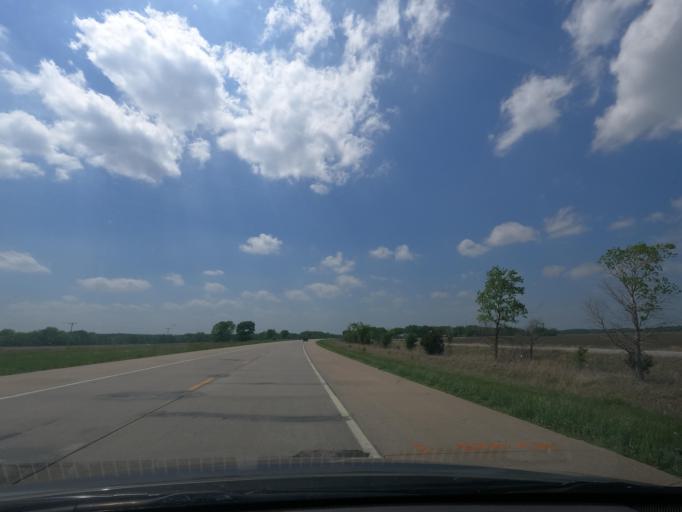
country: US
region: Kansas
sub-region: Wilson County
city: Fredonia
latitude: 37.6195
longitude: -96.0338
